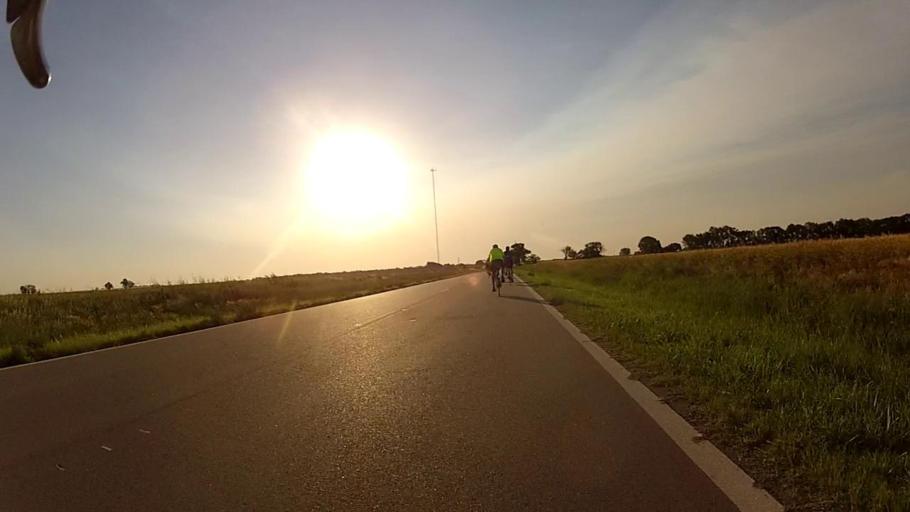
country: US
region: Kansas
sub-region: Harper County
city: Anthony
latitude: 37.1536
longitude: -97.8625
